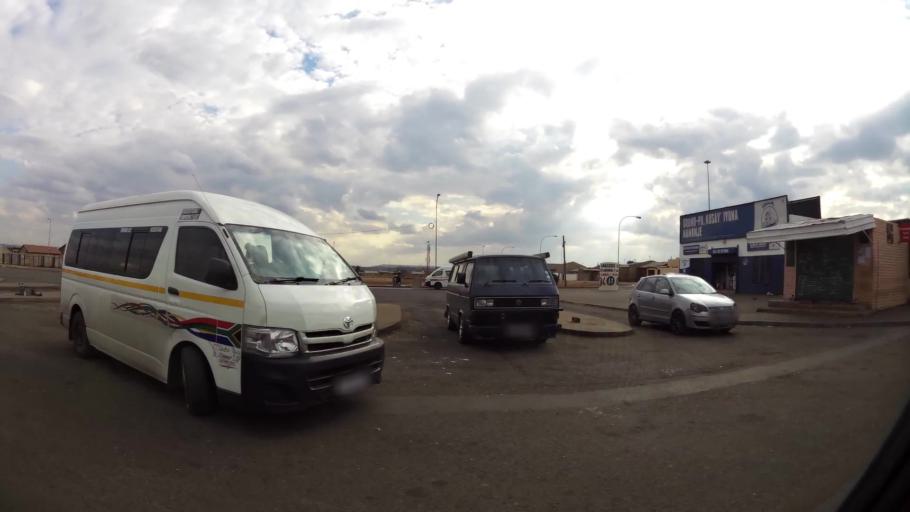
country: ZA
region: Gauteng
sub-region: City of Johannesburg Metropolitan Municipality
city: Soweto
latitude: -26.2469
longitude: 27.8182
